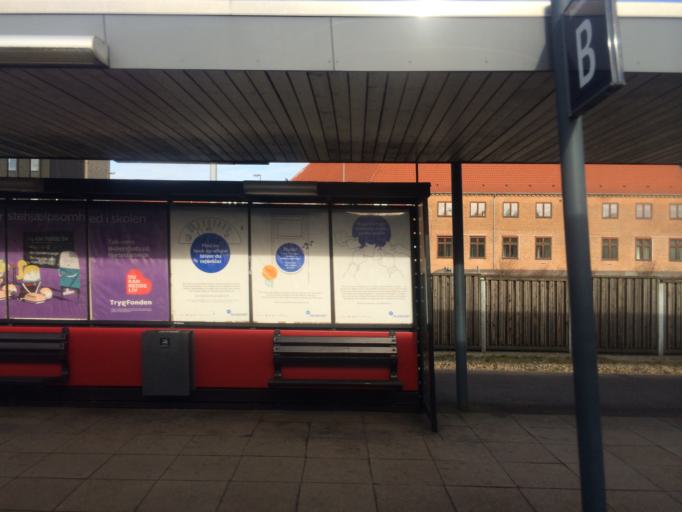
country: DK
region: Central Jutland
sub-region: Herning Kommune
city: Herning
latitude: 56.1325
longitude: 8.9795
